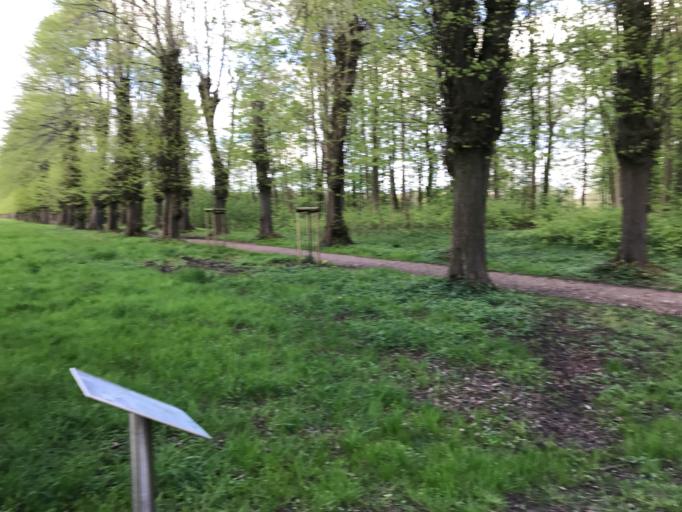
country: DE
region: Schleswig-Holstein
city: Jersbek
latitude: 53.7446
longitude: 10.2240
